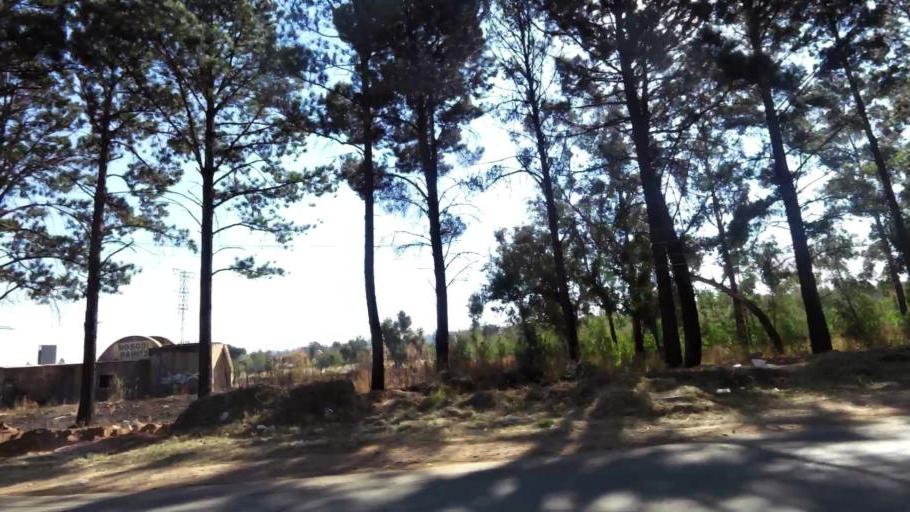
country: ZA
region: Gauteng
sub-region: City of Johannesburg Metropolitan Municipality
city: Johannesburg
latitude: -26.2311
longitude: 27.9984
